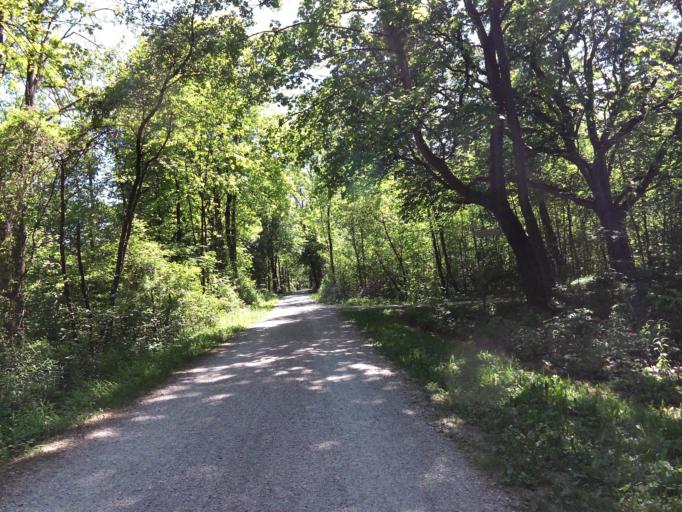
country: DE
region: Bavaria
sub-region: Upper Bavaria
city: Unterfoehring
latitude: 48.2171
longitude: 11.6507
